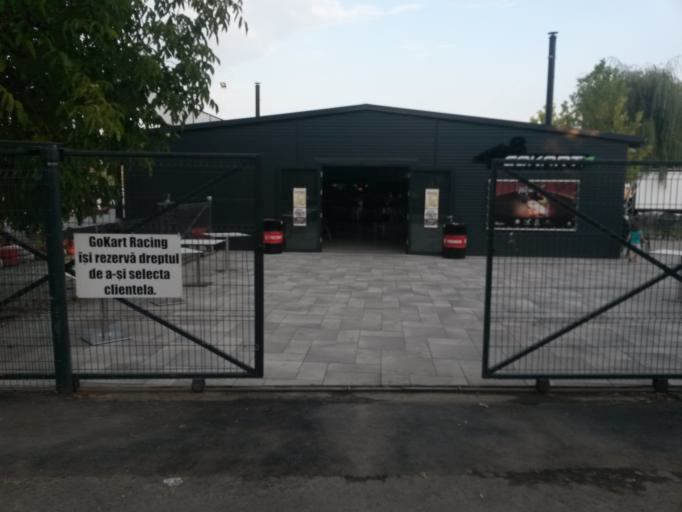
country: RO
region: Mures
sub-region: Comuna Santana de Mures
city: Santana de Mures
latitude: 46.5647
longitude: 24.5705
